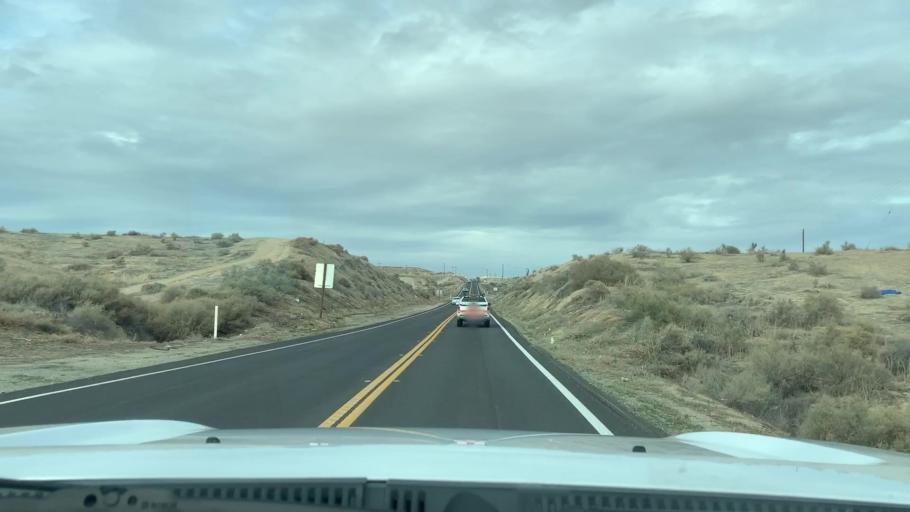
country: US
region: California
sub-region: Kern County
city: South Taft
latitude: 35.1098
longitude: -119.4243
